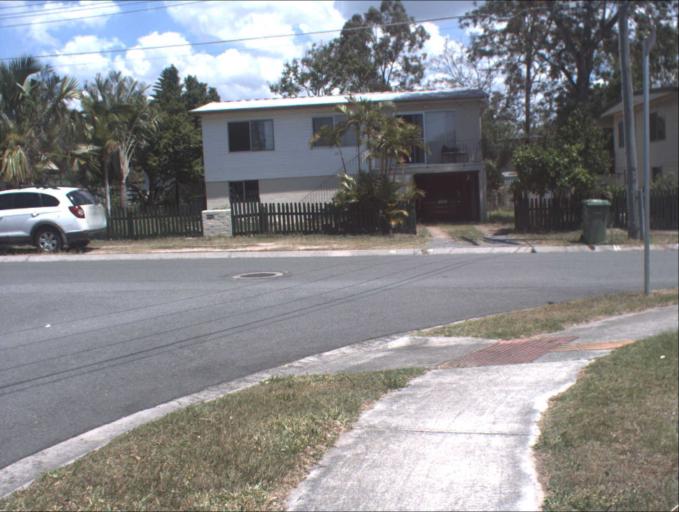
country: AU
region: Queensland
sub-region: Logan
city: Logan City
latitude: -27.6536
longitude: 153.1045
